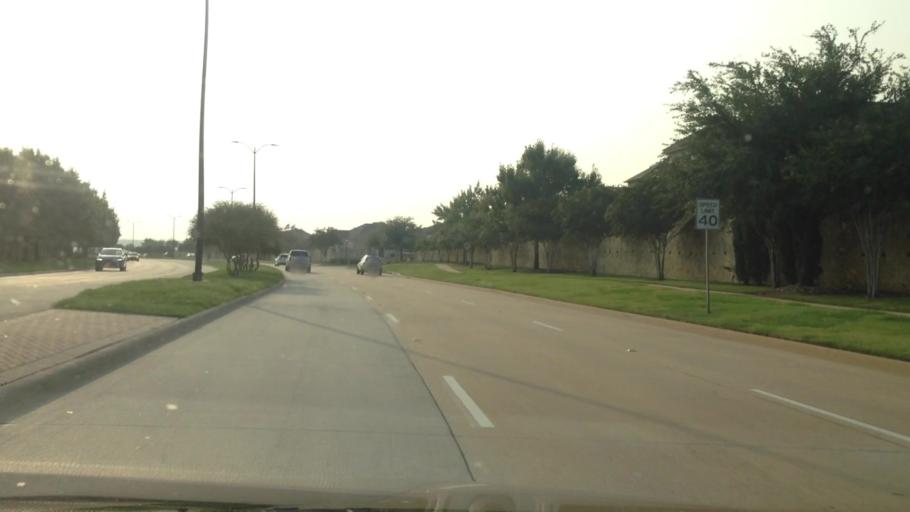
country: US
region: Texas
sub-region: Collin County
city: Frisco
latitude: 33.1315
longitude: -96.8308
